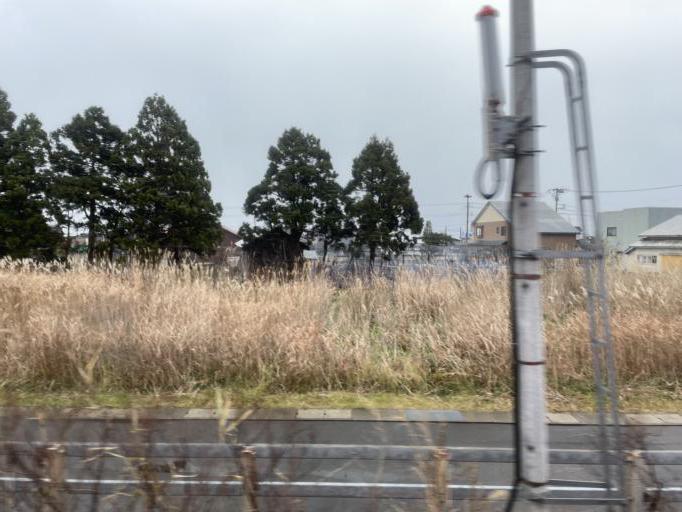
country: JP
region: Aomori
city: Aomori Shi
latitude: 40.9674
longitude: 140.6547
